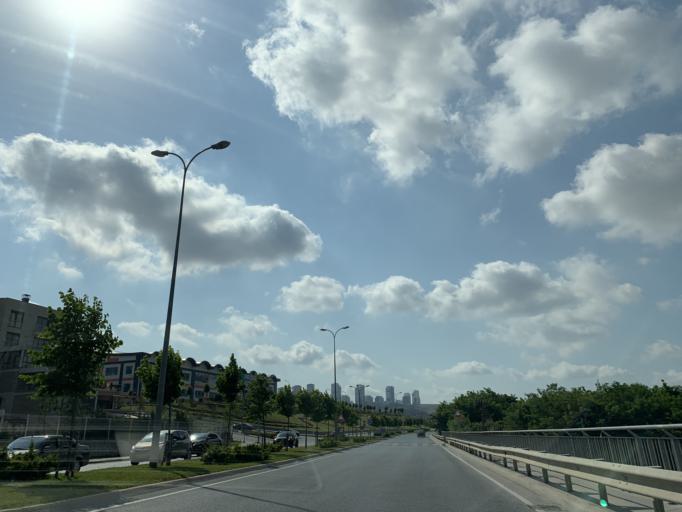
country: TR
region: Istanbul
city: Esenyurt
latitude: 41.0797
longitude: 28.6817
